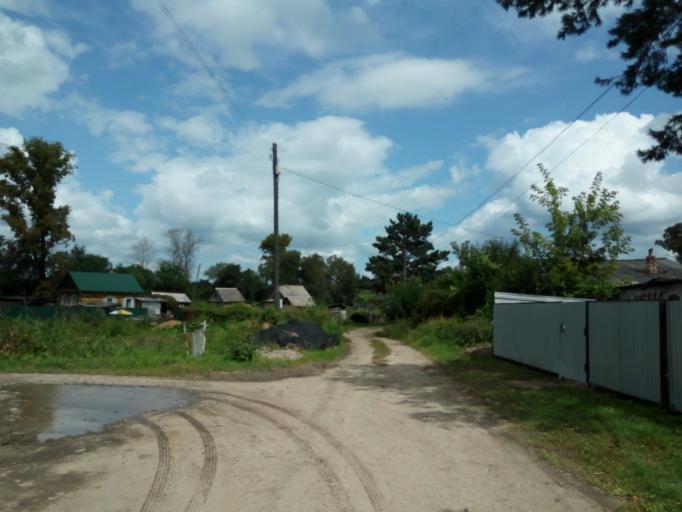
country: RU
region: Primorskiy
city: Dal'nerechensk
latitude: 45.9530
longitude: 133.8099
